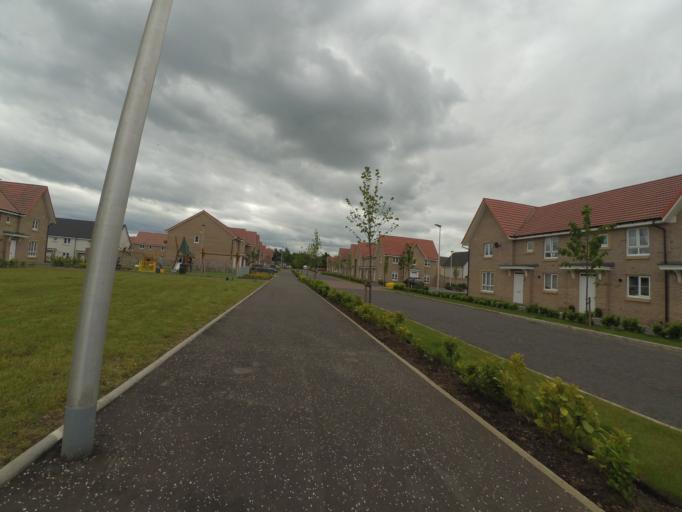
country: GB
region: Scotland
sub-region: East Lothian
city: Musselburgh
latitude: 55.9367
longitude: -3.0909
